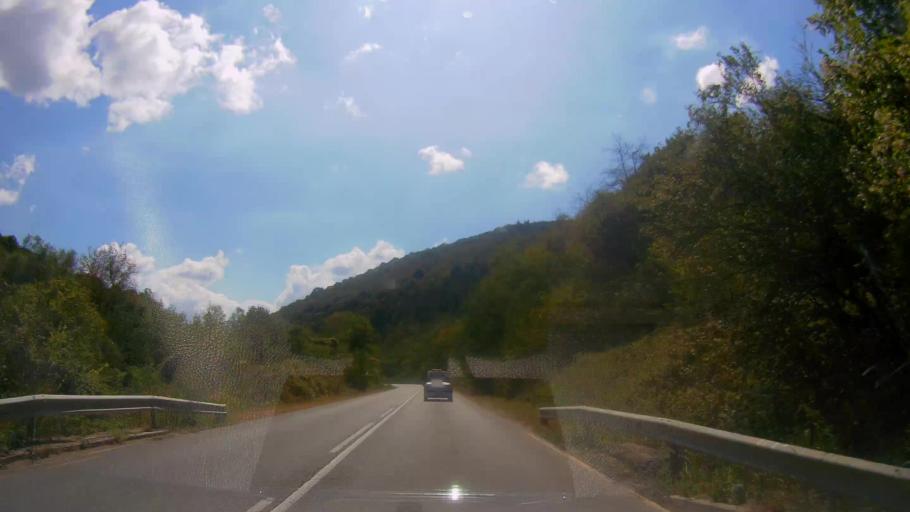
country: BG
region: Stara Zagora
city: Gurkovo
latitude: 42.7383
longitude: 25.7079
